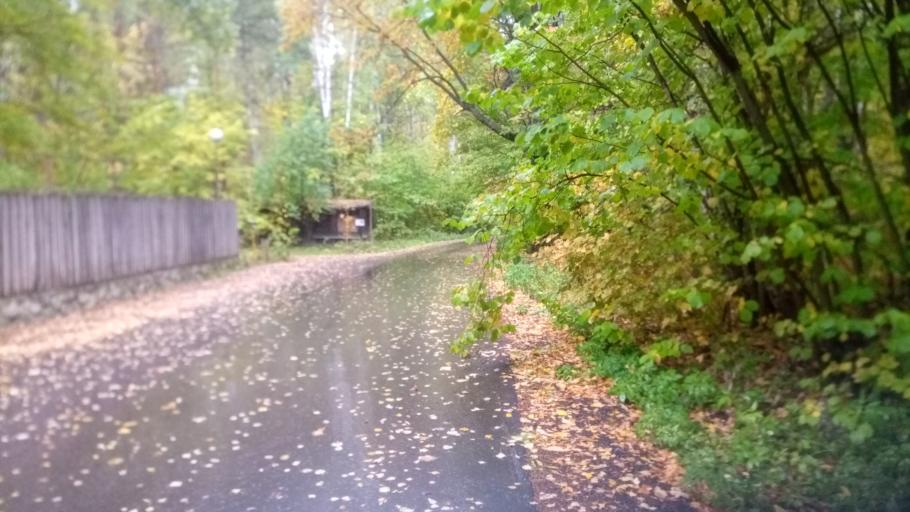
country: RU
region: Tatarstan
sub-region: Tukayevskiy Rayon
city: Naberezhnyye Chelny
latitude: 55.8508
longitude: 52.4624
